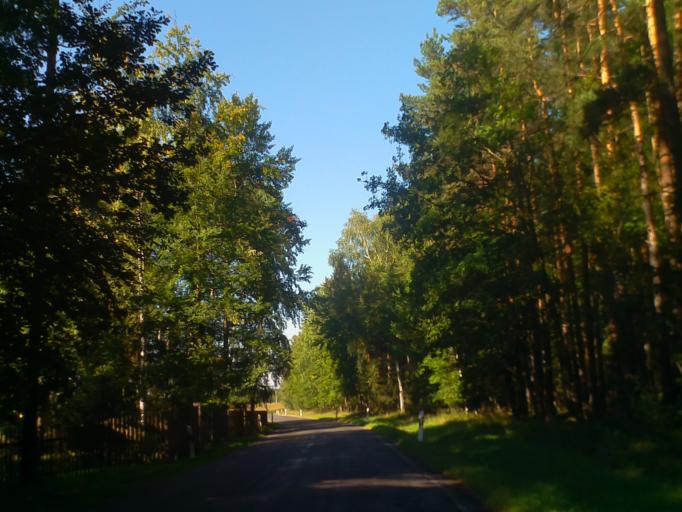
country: DE
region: Thuringia
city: Oberbodnitz
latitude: 50.8018
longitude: 11.6524
